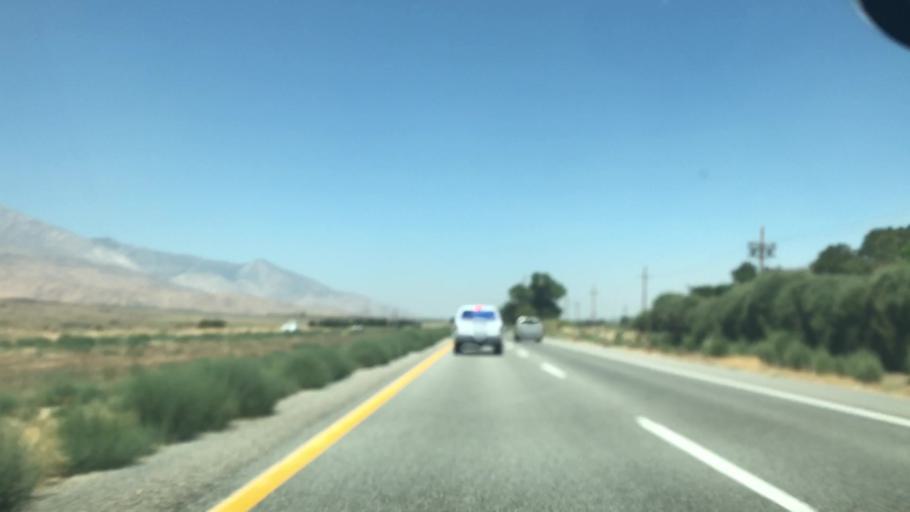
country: US
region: California
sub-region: Inyo County
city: Big Pine
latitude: 37.1331
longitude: -118.2716
